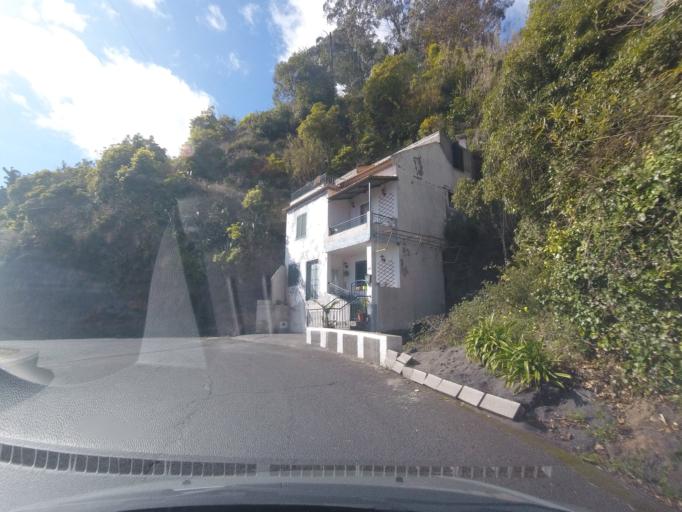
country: PT
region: Madeira
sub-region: Ribeira Brava
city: Campanario
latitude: 32.6631
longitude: -17.0129
